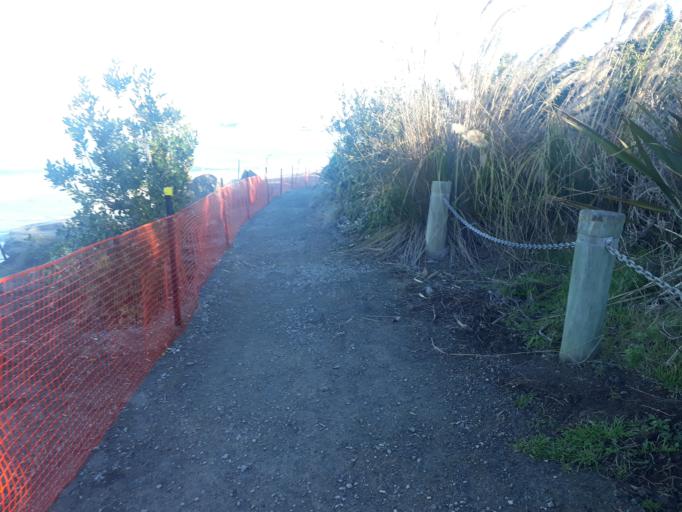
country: NZ
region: Canterbury
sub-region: Timaru District
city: Timaru
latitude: -44.4154
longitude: 171.2639
